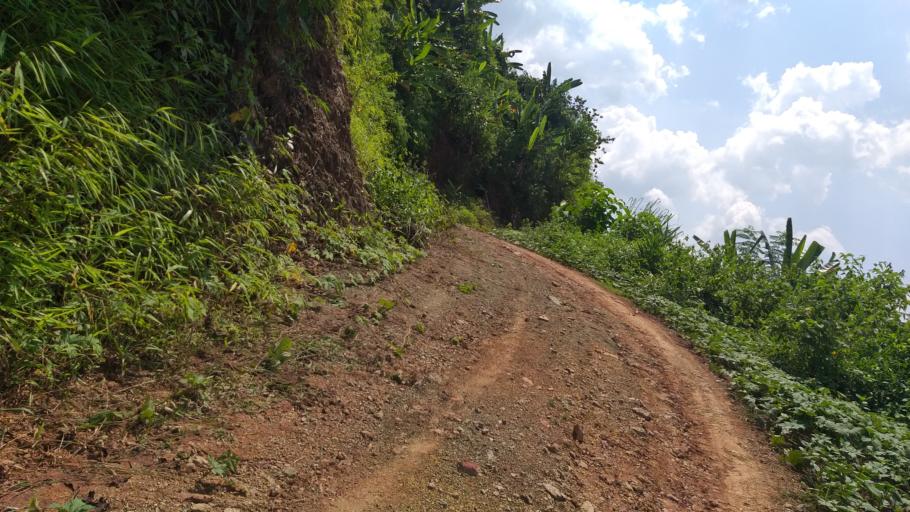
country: LA
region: Phongsali
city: Khoa
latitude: 21.2989
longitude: 102.5494
